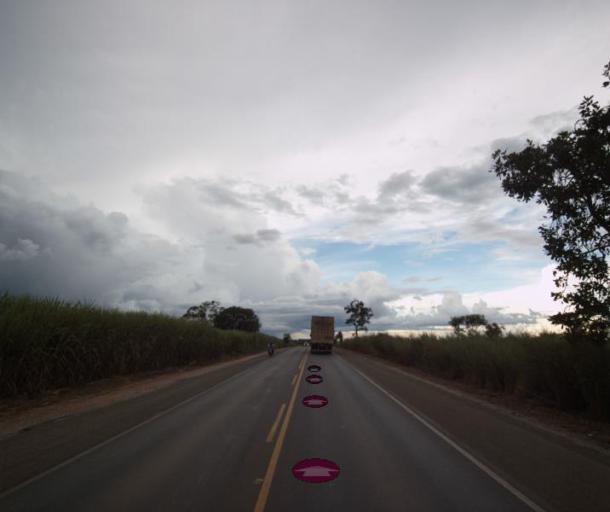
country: BR
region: Goias
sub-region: Itapaci
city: Itapaci
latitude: -14.9266
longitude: -49.3634
